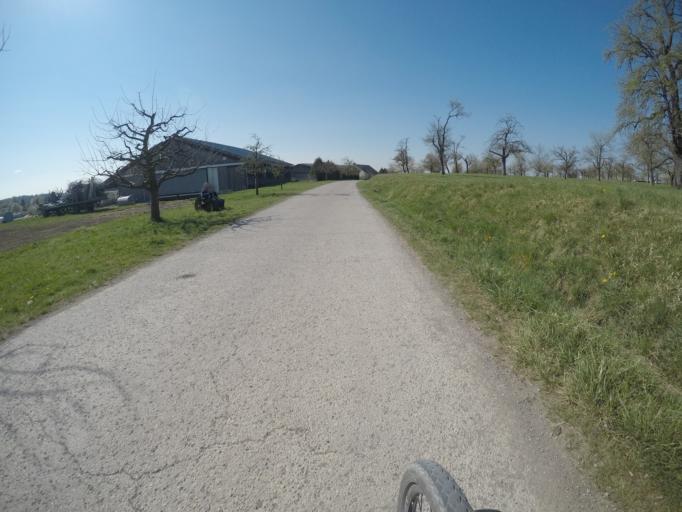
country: DE
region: Baden-Wuerttemberg
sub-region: Regierungsbezirk Stuttgart
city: Herrenberg
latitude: 48.5665
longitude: 8.9231
